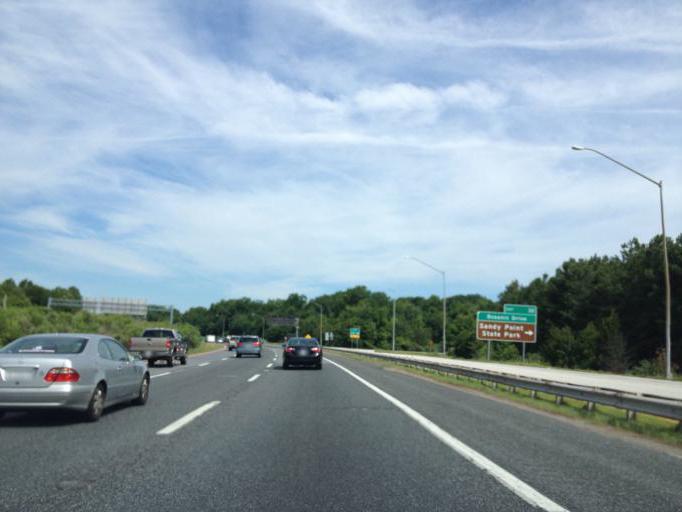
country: US
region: Maryland
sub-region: Anne Arundel County
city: Cape Saint Claire
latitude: 39.0175
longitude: -76.4099
